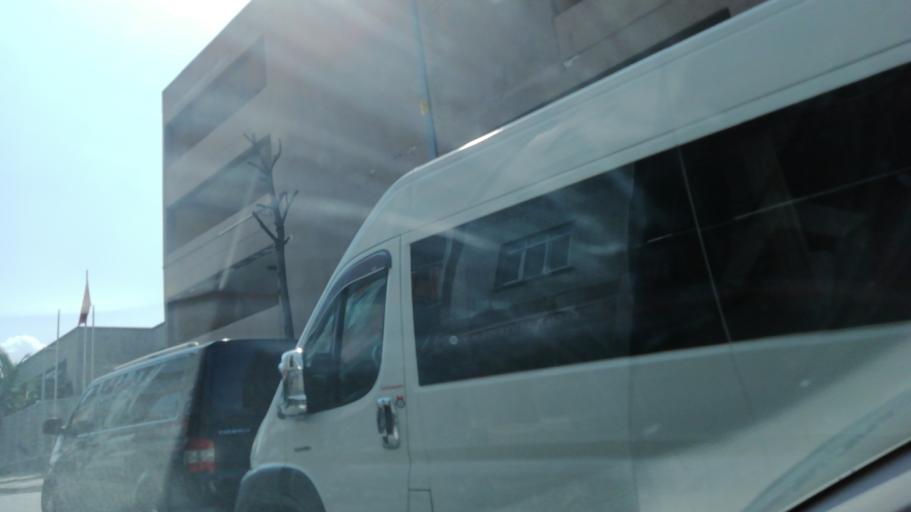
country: TR
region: Istanbul
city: Mahmutbey
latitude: 41.0327
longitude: 28.8203
